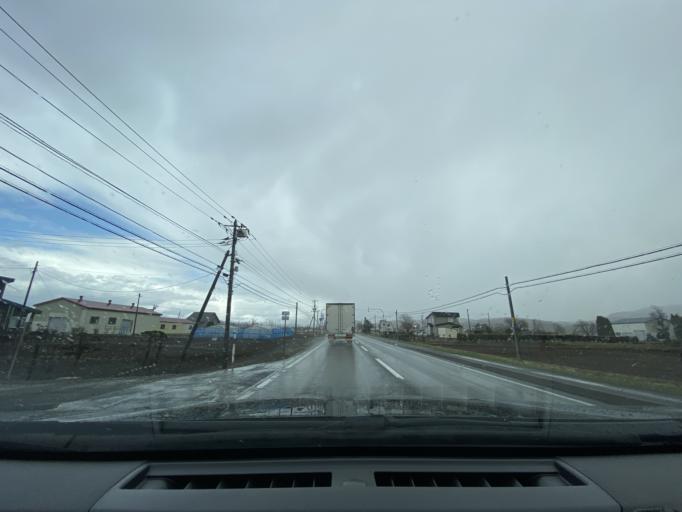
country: JP
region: Hokkaido
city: Fukagawa
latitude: 43.6694
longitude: 142.0117
